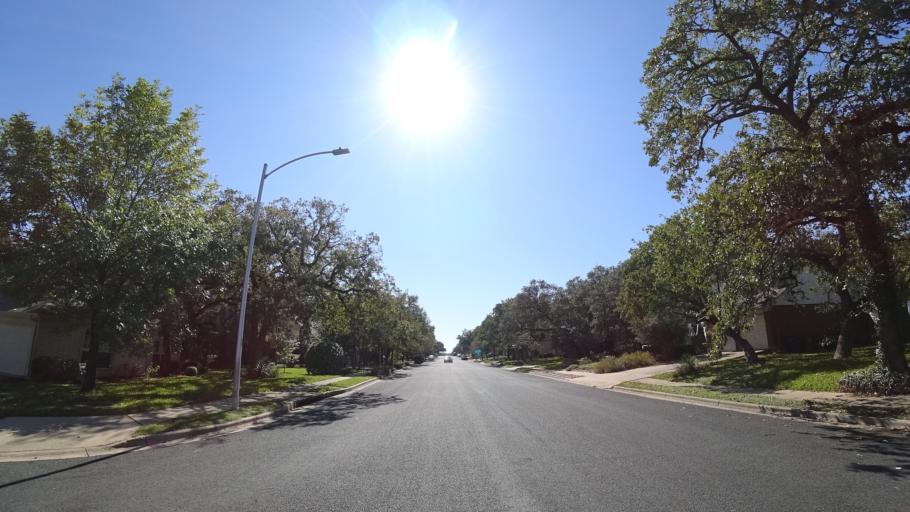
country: US
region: Texas
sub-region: Travis County
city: Shady Hollow
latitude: 30.2183
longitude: -97.8702
